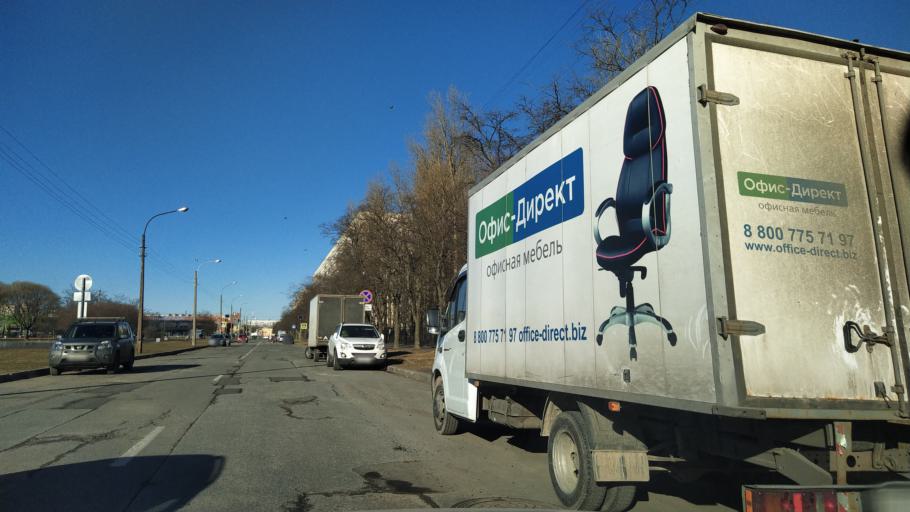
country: RU
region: St.-Petersburg
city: Grazhdanka
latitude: 60.0382
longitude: 30.3895
